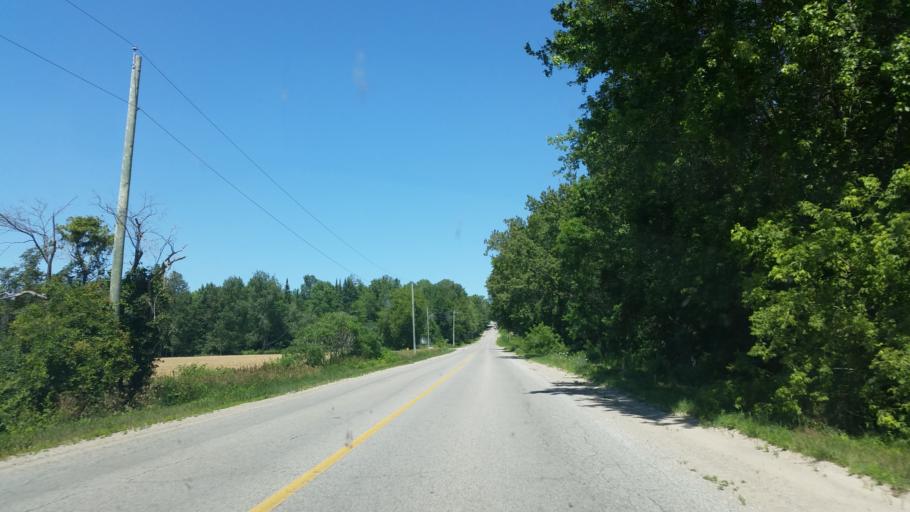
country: CA
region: Ontario
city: Barrie
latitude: 44.4624
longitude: -79.7962
